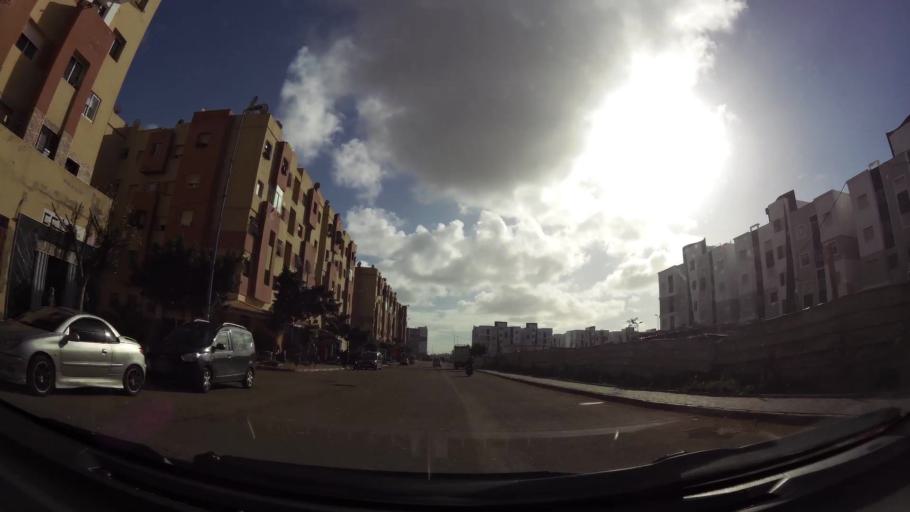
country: MA
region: Grand Casablanca
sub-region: Casablanca
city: Casablanca
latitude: 33.5518
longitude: -7.7046
